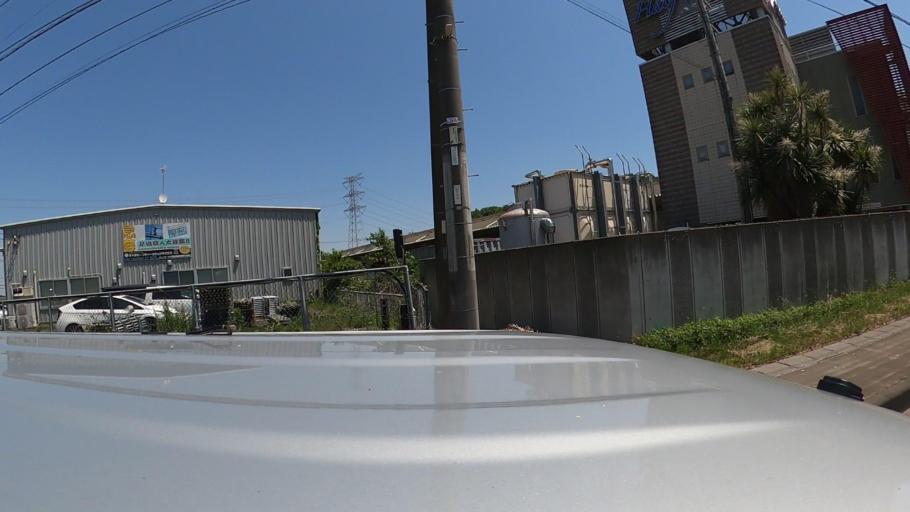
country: JP
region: Ibaraki
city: Ushiku
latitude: 36.0144
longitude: 140.0831
